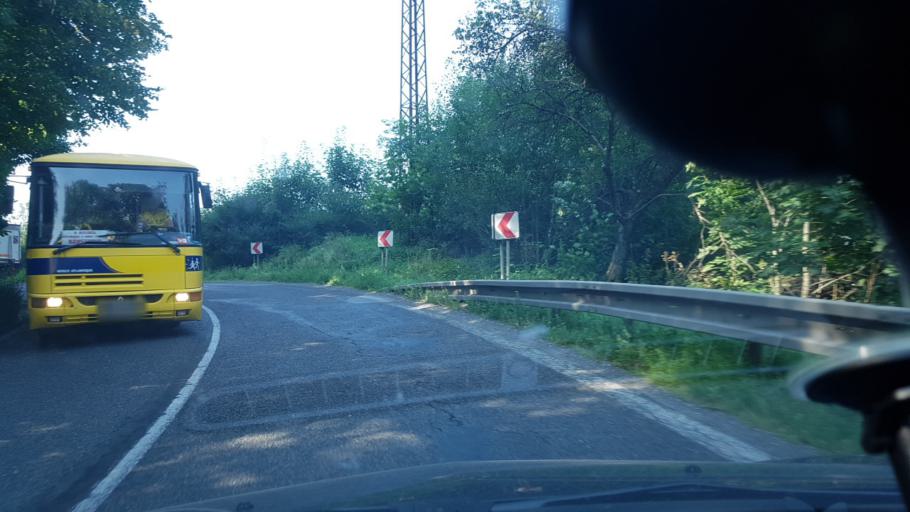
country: SK
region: Zilinsky
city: Tvrdosin
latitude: 49.3048
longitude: 19.4811
